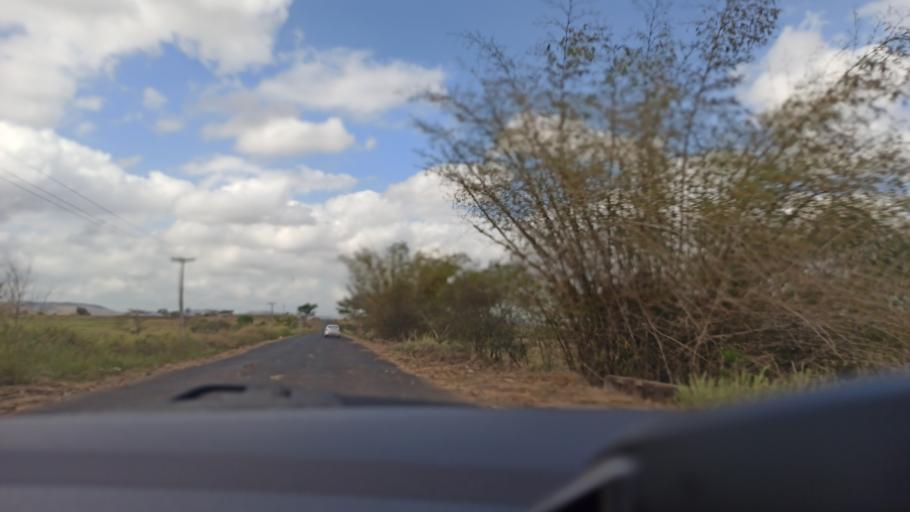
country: BR
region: Pernambuco
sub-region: Timbauba
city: Timbauba
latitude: -7.4754
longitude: -35.2800
